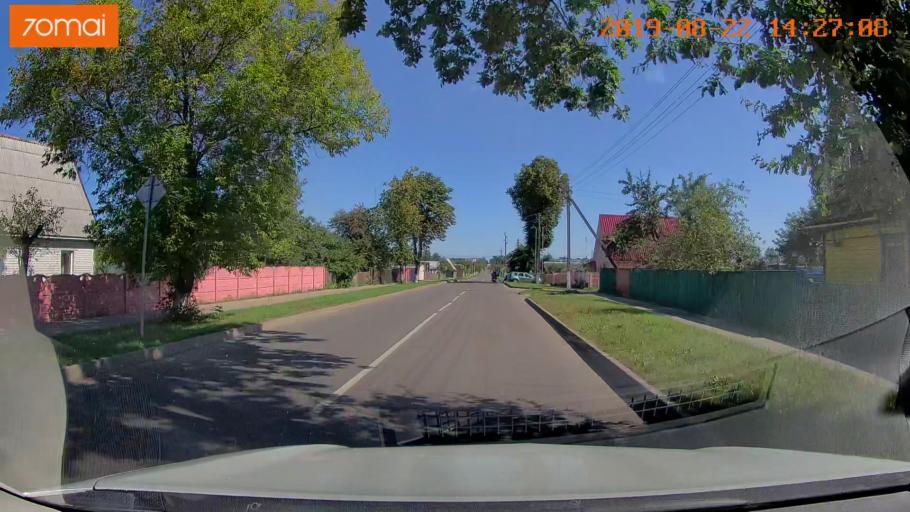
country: BY
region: Mogilev
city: Asipovichy
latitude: 53.2976
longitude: 28.6225
